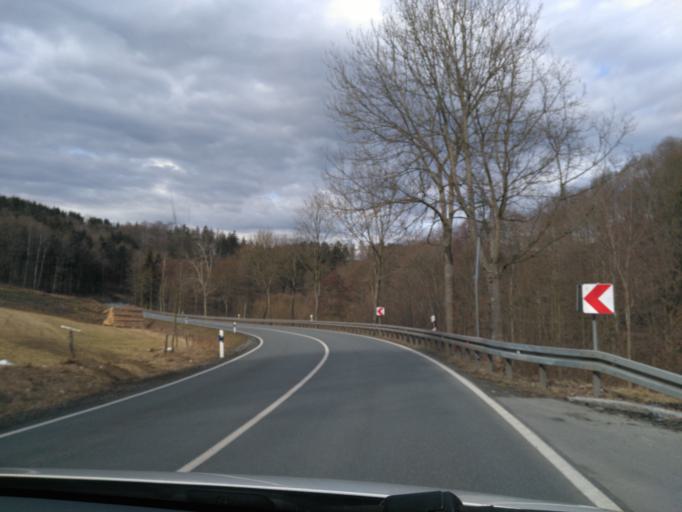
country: DE
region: Saxony
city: Wolkenstein
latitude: 50.6571
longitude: 13.0614
